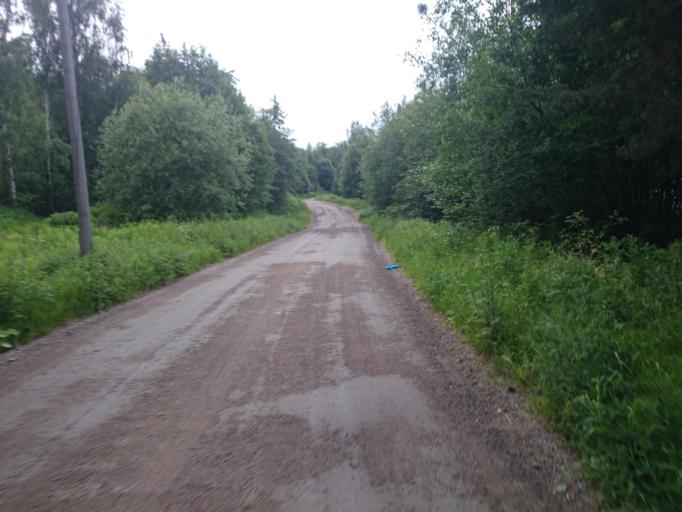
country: SE
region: Vaesternorrland
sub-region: Sundsvalls Kommun
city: Kvissleby
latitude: 62.3040
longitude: 17.3764
